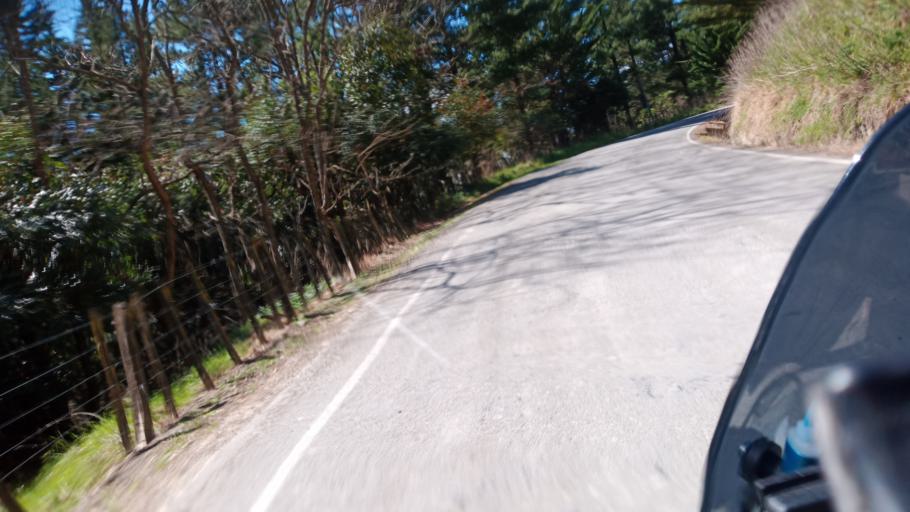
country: NZ
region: Gisborne
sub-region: Gisborne District
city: Gisborne
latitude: -38.7931
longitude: 177.7759
